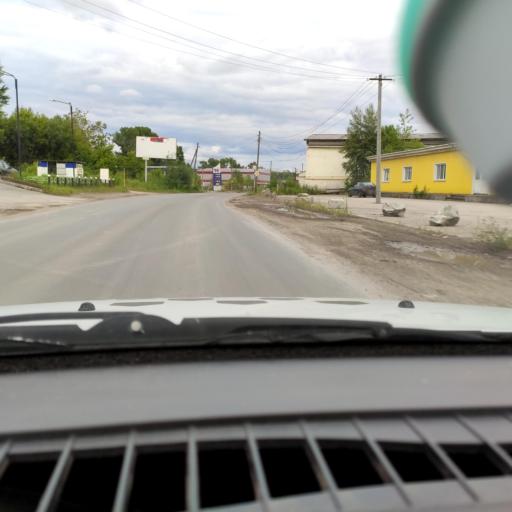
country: RU
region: Perm
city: Chusovoy
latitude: 58.3009
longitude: 57.8117
